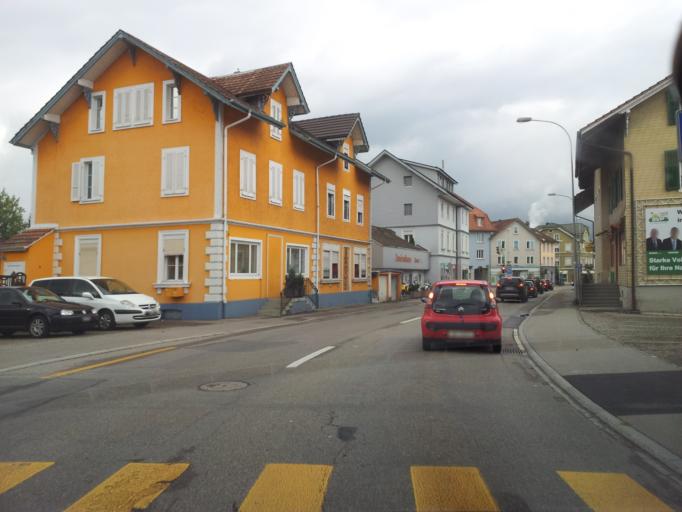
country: CH
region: Solothurn
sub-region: Bezirk Wasseramt
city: Derendingen
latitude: 47.1990
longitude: 7.5822
